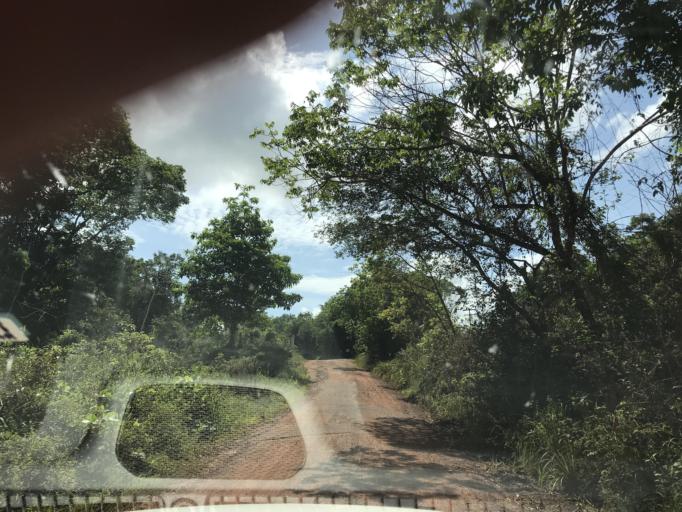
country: BR
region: Bahia
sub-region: Entre Rios
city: Entre Rios
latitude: -12.1681
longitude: -38.0691
